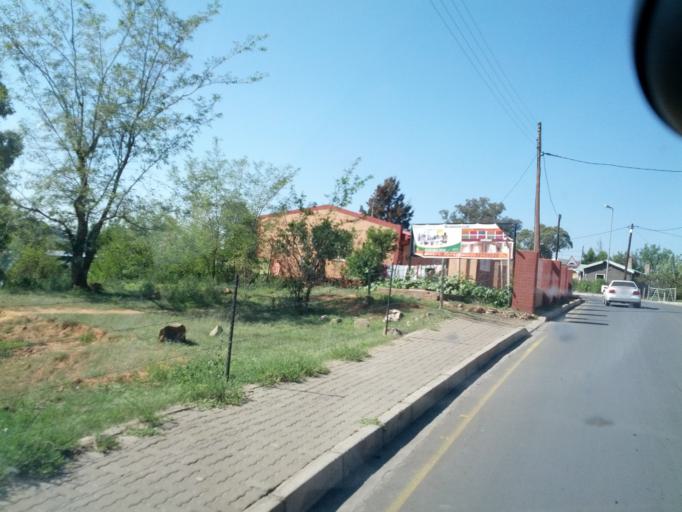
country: LS
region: Maseru
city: Maseru
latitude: -29.3038
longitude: 27.4939
